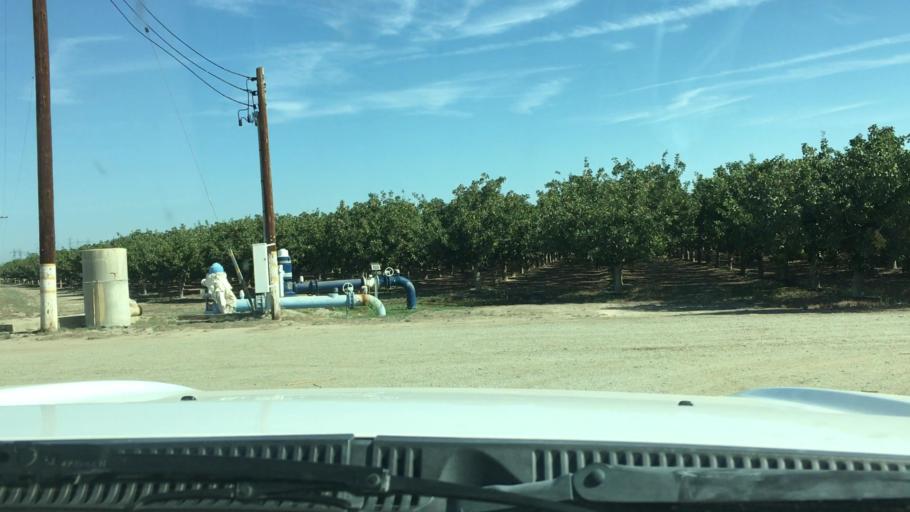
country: US
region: California
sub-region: Kern County
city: Buttonwillow
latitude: 35.3729
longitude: -119.4014
